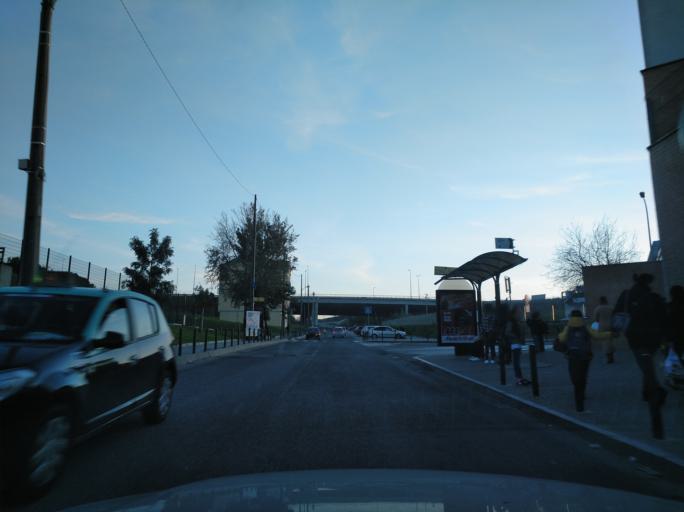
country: PT
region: Lisbon
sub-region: Odivelas
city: Olival do Basto
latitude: 38.7908
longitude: -9.1507
